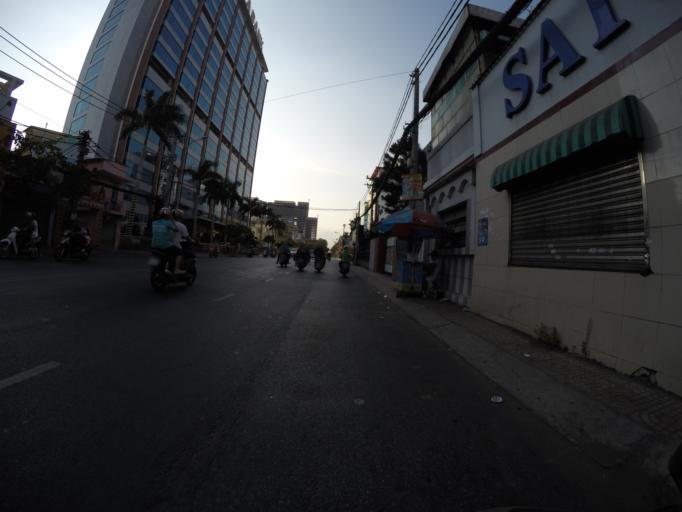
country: VN
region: Ho Chi Minh City
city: Quan Ba
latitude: 10.7757
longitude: 106.6858
